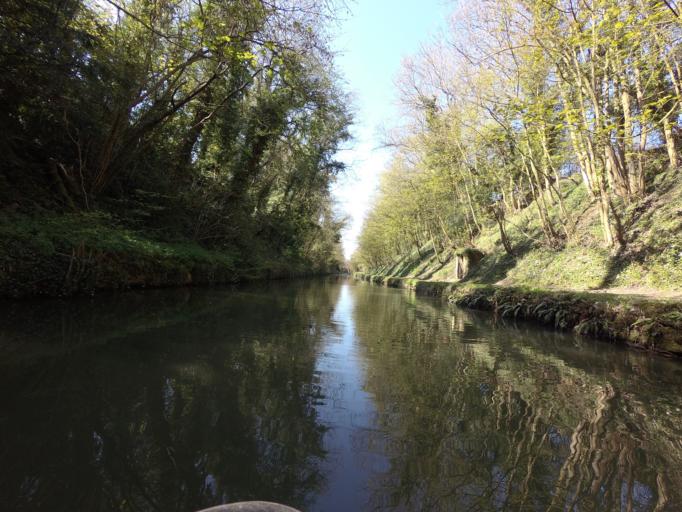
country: GB
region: England
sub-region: Hertfordshire
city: Tring
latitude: 51.8053
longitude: -0.6376
